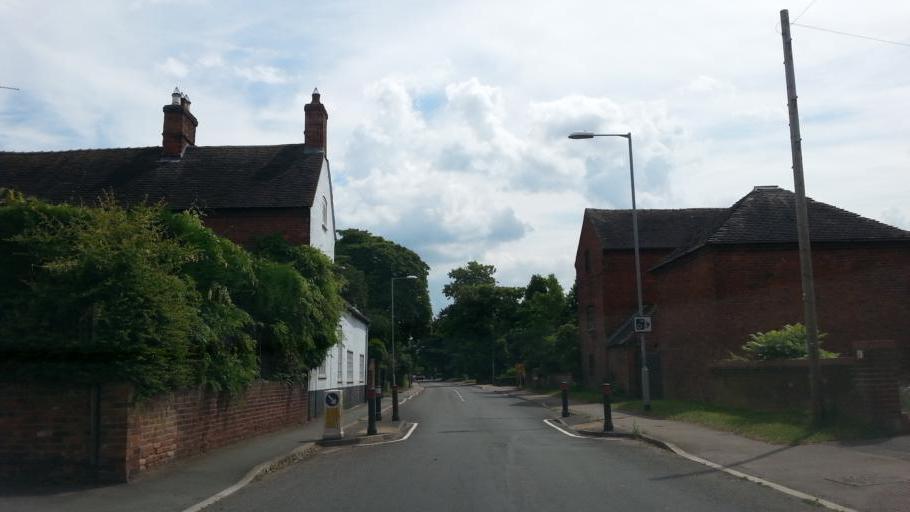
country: GB
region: England
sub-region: Staffordshire
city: Armitage
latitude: 52.7488
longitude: -1.8178
